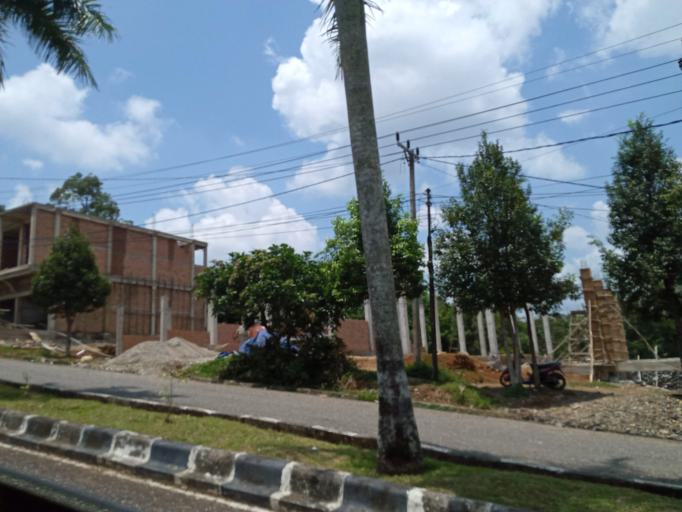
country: ID
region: Jambi
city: Bangko
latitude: -2.0552
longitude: 102.2809
